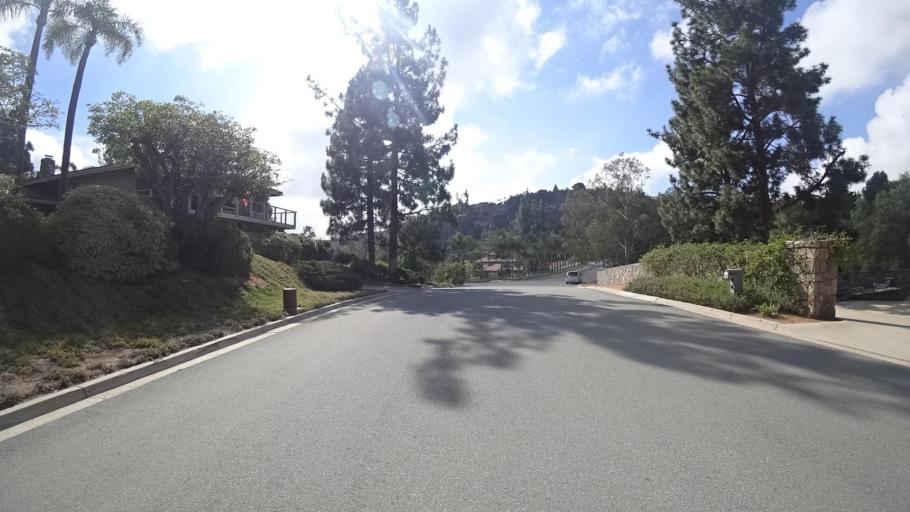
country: US
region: California
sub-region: San Diego County
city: Granite Hills
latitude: 32.7790
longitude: -116.8955
